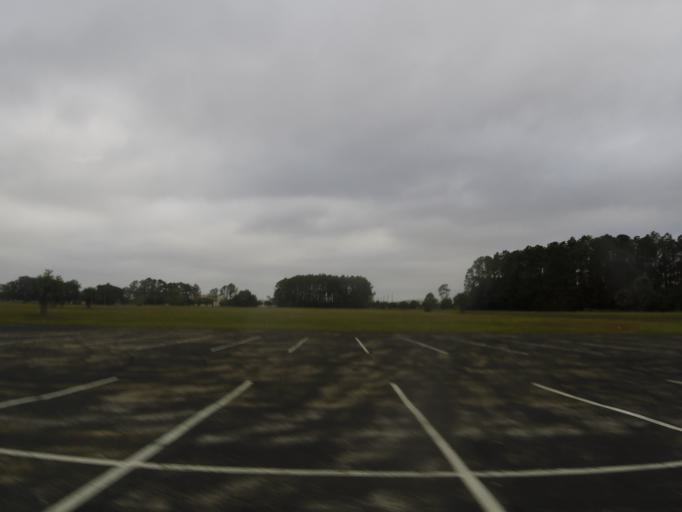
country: US
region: Florida
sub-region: Duval County
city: Baldwin
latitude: 30.2302
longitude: -81.8860
